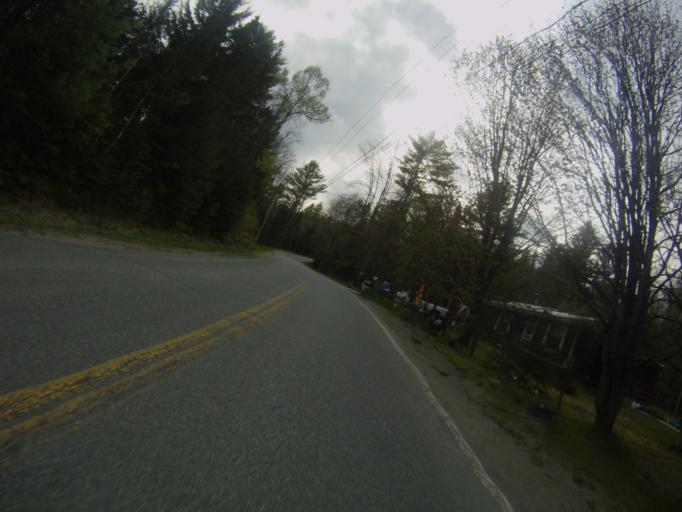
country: US
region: New York
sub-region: Warren County
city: Warrensburg
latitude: 43.8405
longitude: -73.8583
